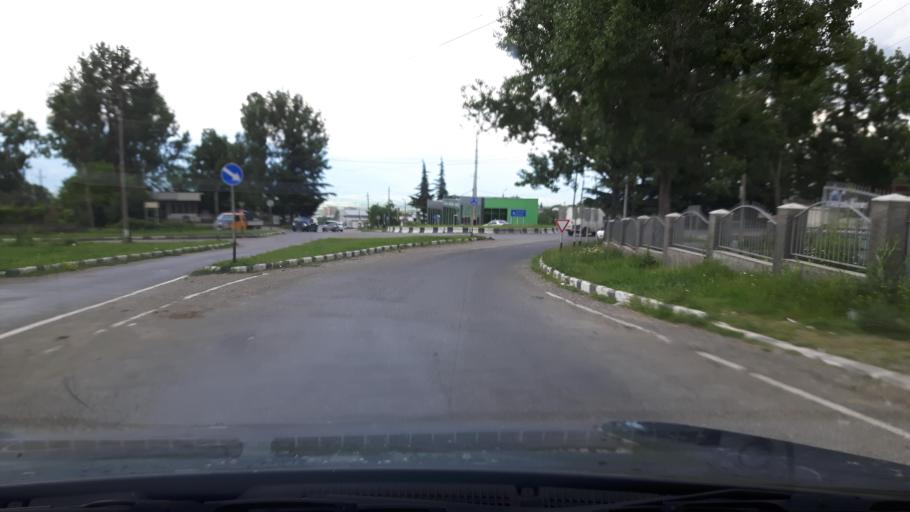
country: GE
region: Kakheti
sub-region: Telavi
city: Telavi
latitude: 41.9258
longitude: 45.4533
